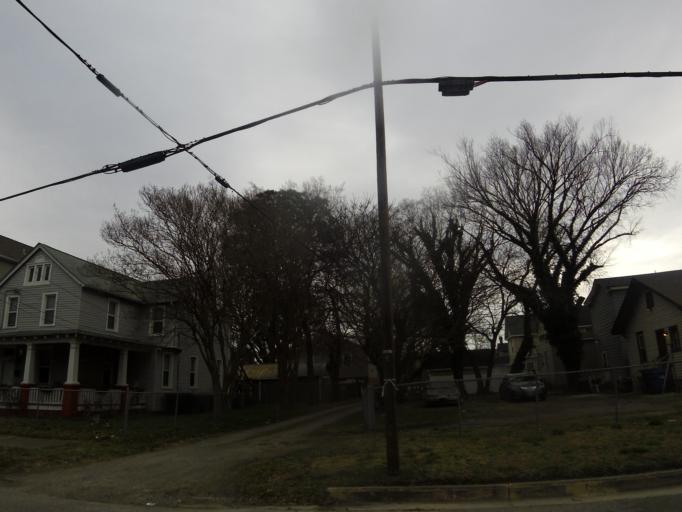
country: US
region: Virginia
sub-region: City of Portsmouth
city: Portsmouth
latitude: 36.8336
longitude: -76.3239
